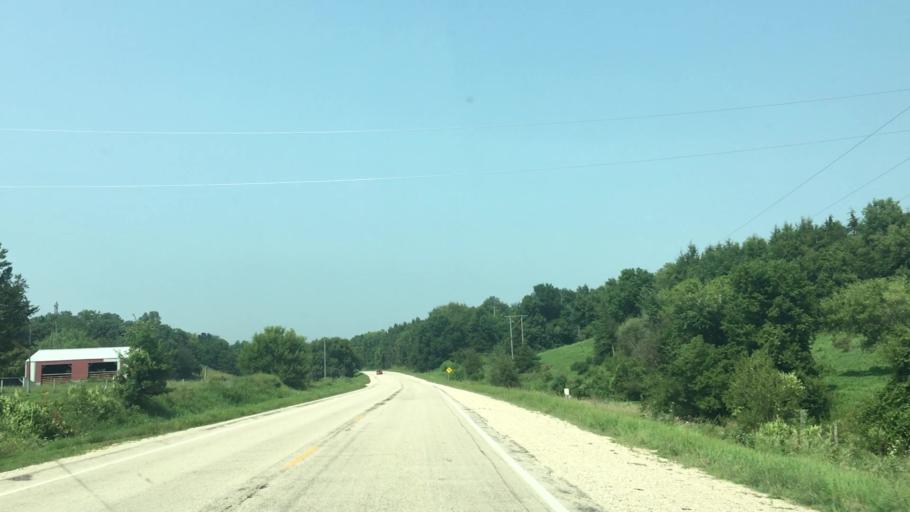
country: US
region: Iowa
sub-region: Fayette County
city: West Union
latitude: 43.0704
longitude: -91.8388
